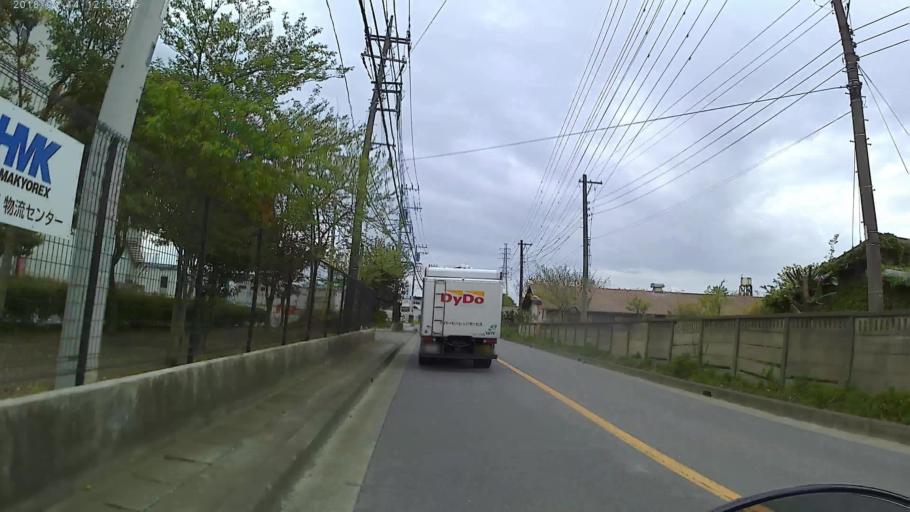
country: JP
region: Kanagawa
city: Atsugi
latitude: 35.4168
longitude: 139.4078
